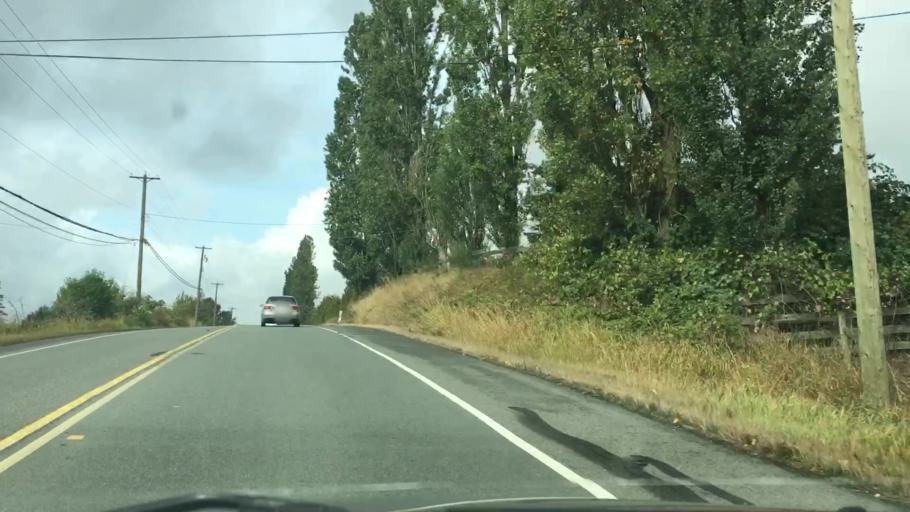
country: CA
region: British Columbia
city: Langley
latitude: 49.1044
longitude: -122.5931
